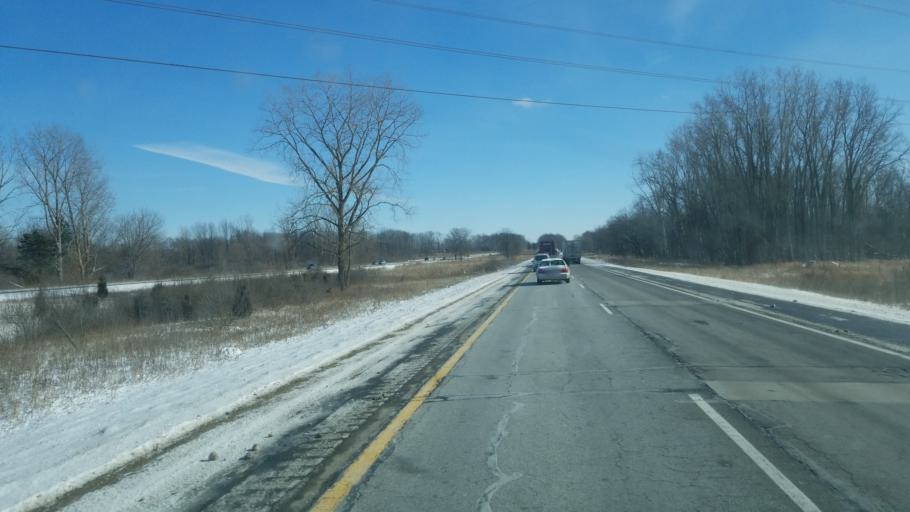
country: US
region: Michigan
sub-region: Livingston County
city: Fowlerville
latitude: 42.6413
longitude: -84.0388
